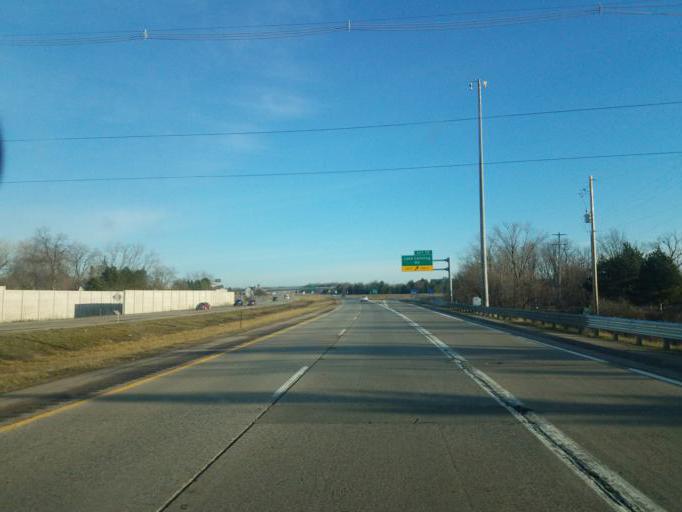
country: US
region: Michigan
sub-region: Ingham County
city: East Lansing
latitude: 42.7552
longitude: -84.5078
